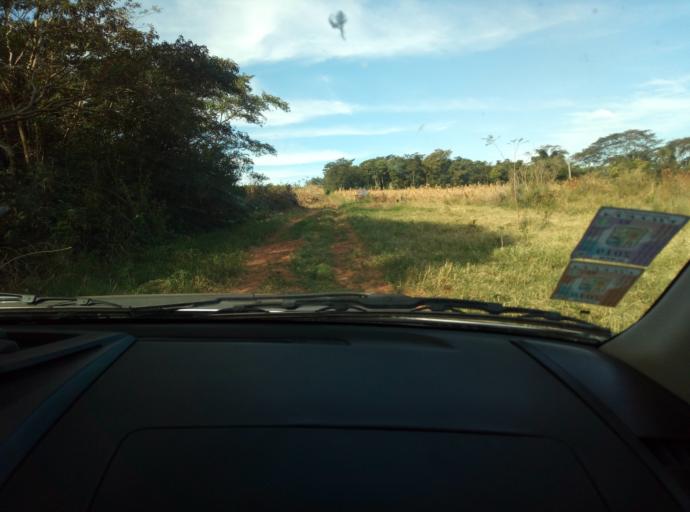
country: PY
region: Caaguazu
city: Carayao
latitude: -25.1727
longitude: -56.2836
